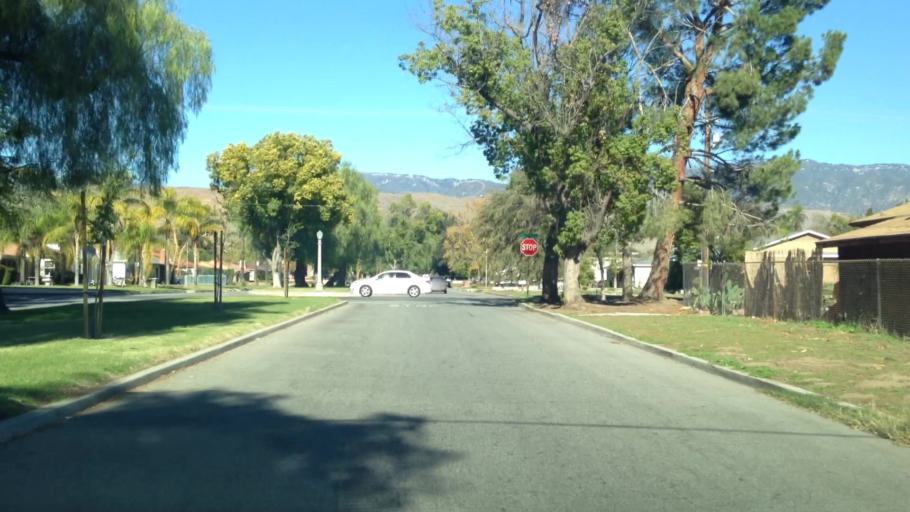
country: US
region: California
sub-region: San Bernardino County
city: San Bernardino
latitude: 34.1402
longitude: -117.3077
